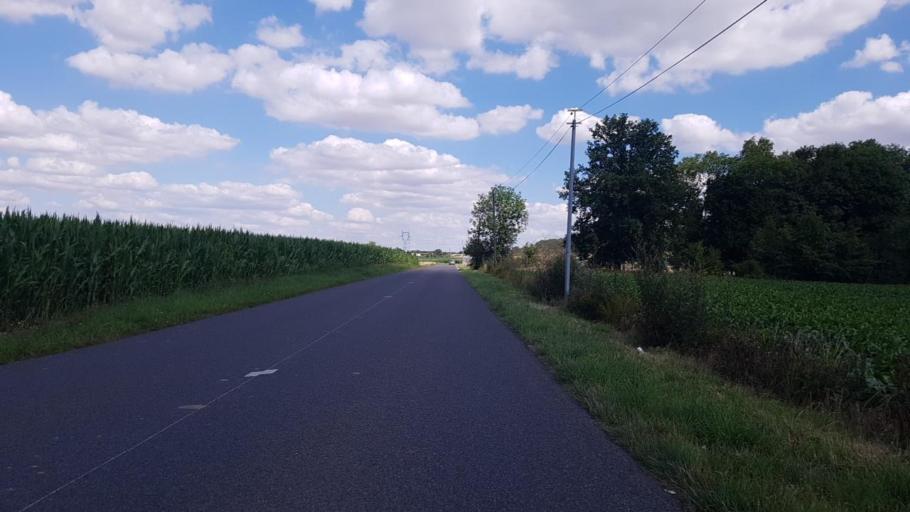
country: FR
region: Ile-de-France
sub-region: Departement de Seine-et-Marne
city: Moussy-le-Vieux
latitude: 49.0699
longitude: 2.6301
